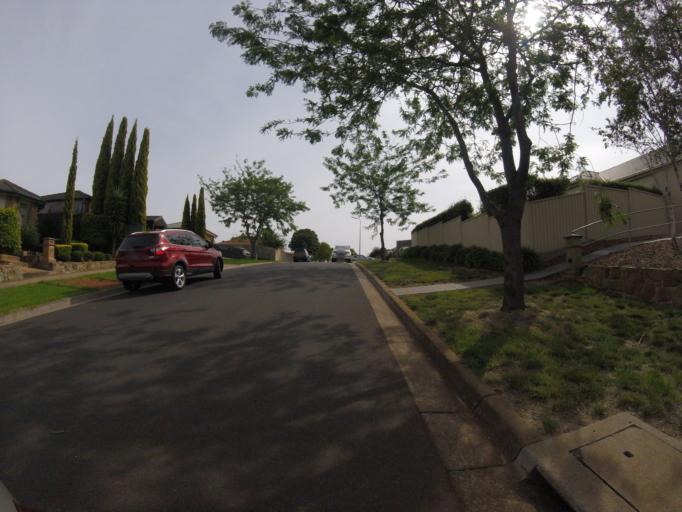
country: AU
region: Victoria
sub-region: Hume
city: Meadow Heights
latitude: -37.6501
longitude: 144.9022
